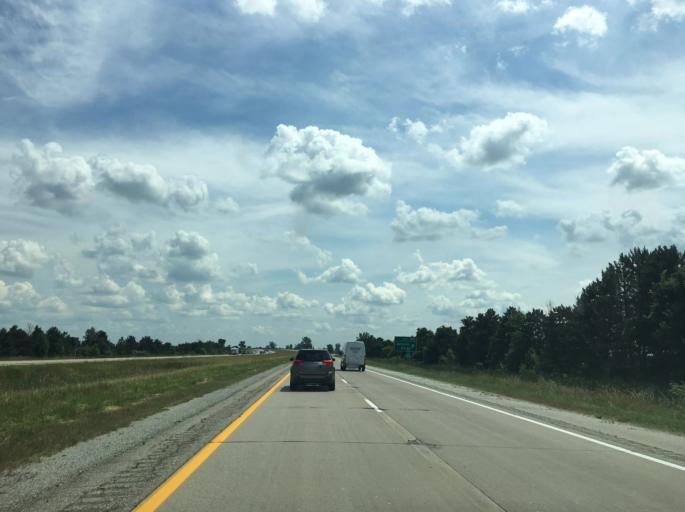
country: US
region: Michigan
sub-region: Bay County
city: Auburn
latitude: 43.6759
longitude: -84.0133
